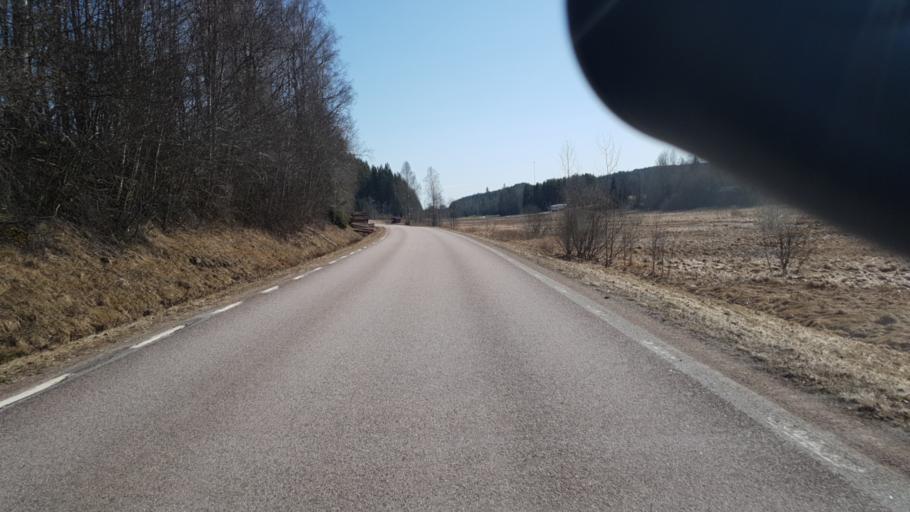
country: SE
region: Vaermland
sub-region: Arvika Kommun
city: Arvika
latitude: 59.6711
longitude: 12.7970
